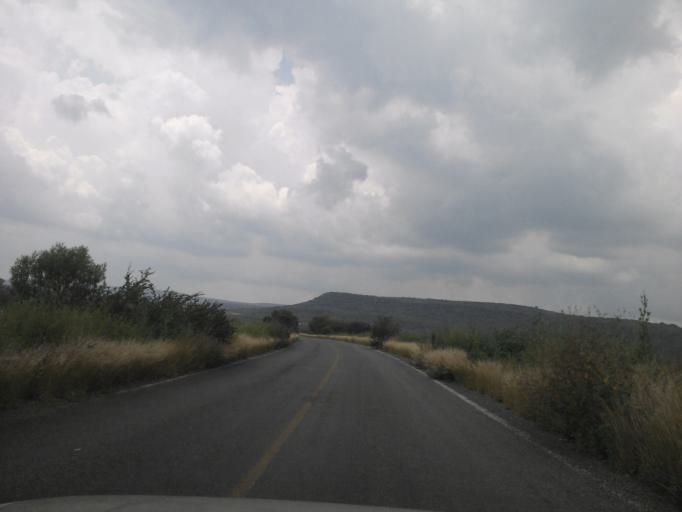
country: MX
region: Jalisco
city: San Diego de Alejandria
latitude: 20.8933
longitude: -101.9693
